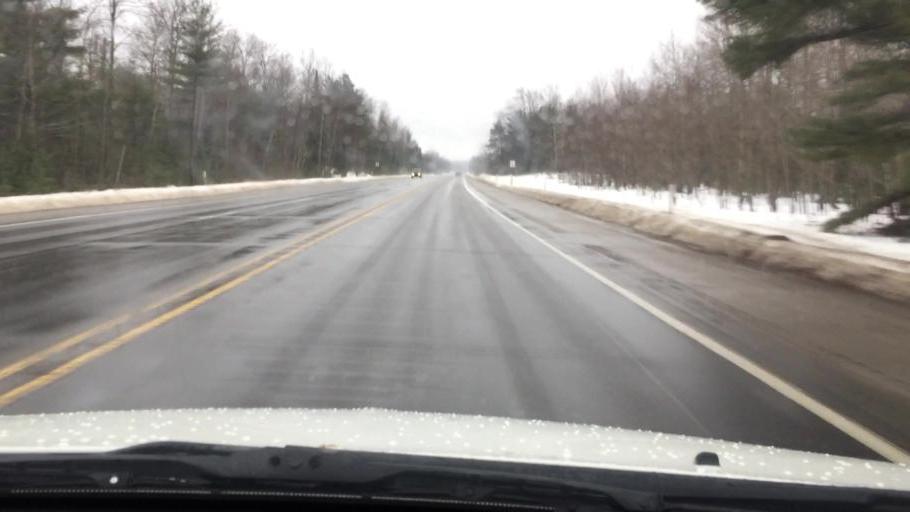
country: US
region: Michigan
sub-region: Kalkaska County
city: Kalkaska
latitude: 44.6647
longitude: -85.2474
